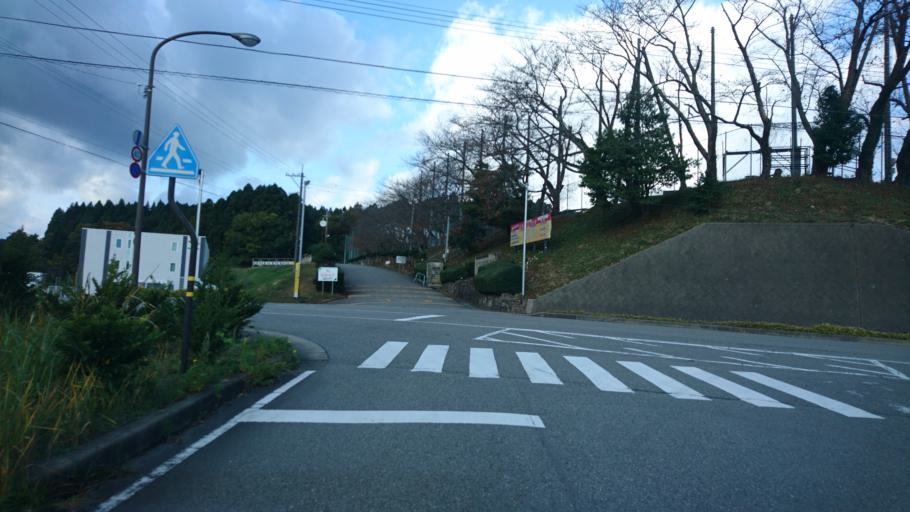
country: JP
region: Fukui
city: Maruoka
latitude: 36.2966
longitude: 136.3064
